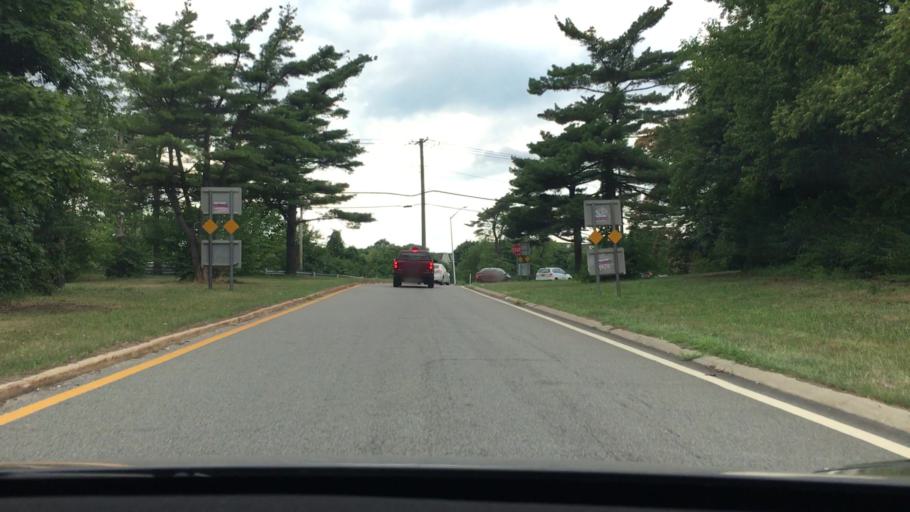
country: US
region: New York
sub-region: Nassau County
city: East Garden City
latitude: 40.7377
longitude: -73.5925
